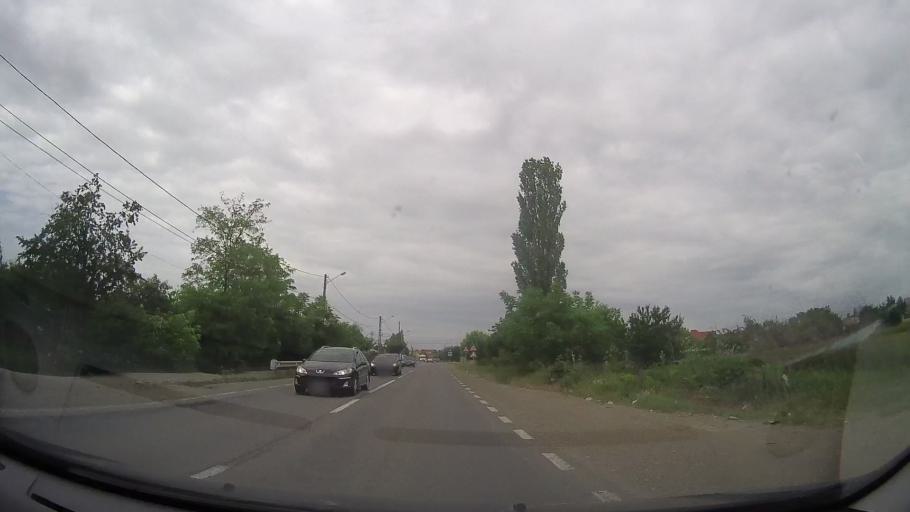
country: RO
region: Prahova
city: Ploiesti
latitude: 44.9631
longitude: 26.0369
